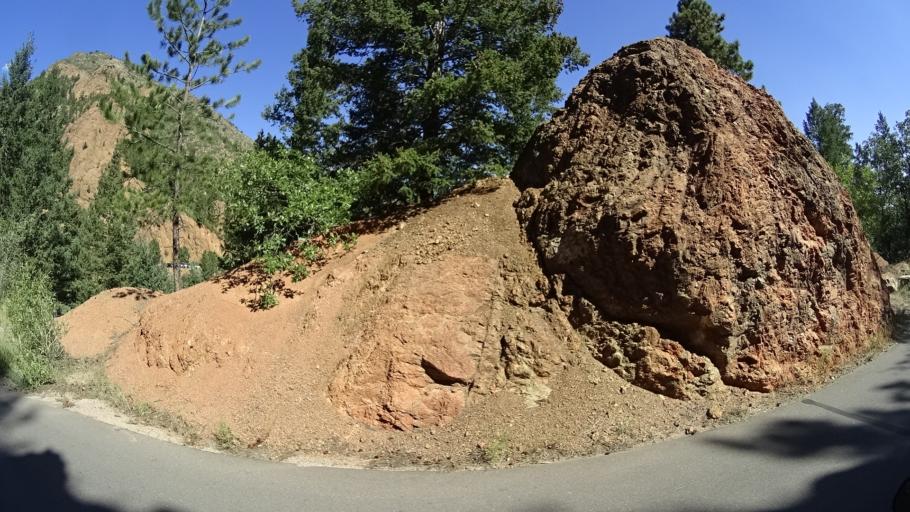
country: US
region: Colorado
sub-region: El Paso County
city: Manitou Springs
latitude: 38.8205
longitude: -104.8900
